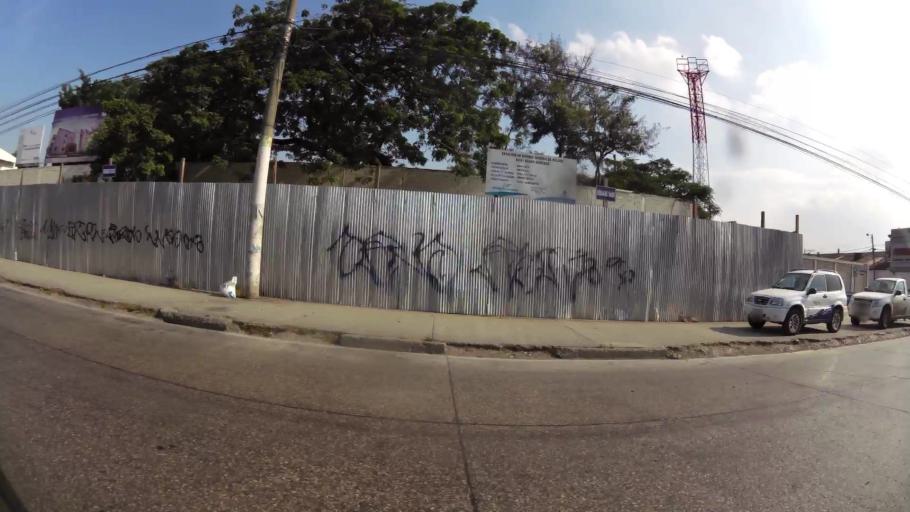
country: EC
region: Guayas
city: Guayaquil
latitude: -2.1415
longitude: -79.9250
